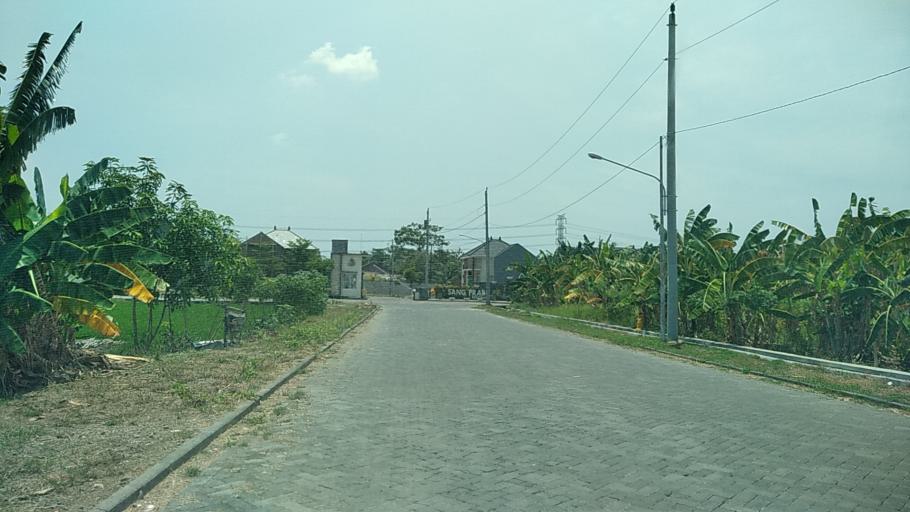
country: ID
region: Central Java
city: Mranggen
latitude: -7.0102
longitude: 110.4857
